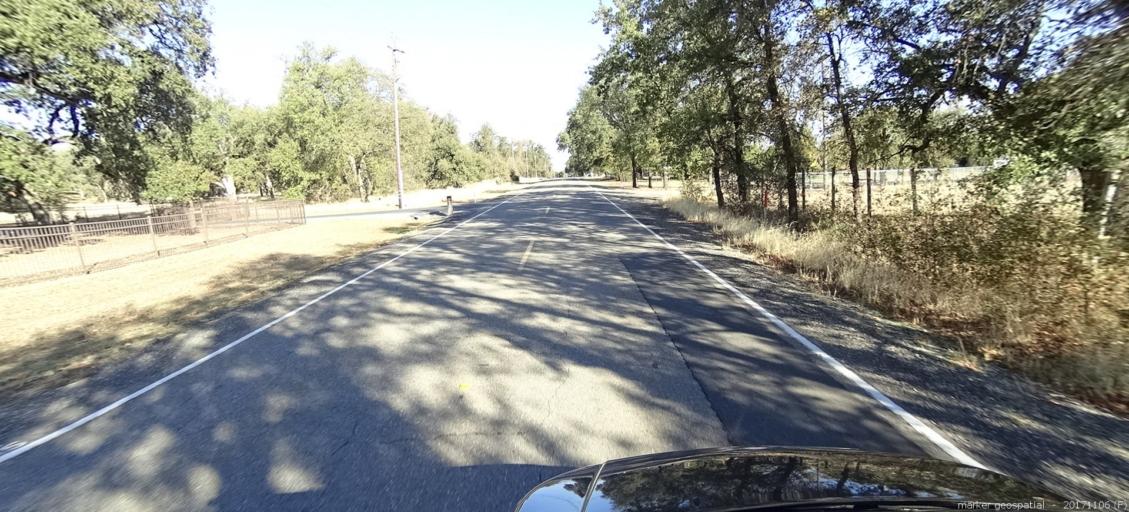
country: US
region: California
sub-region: Shasta County
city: Palo Cedro
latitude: 40.5125
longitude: -122.2385
